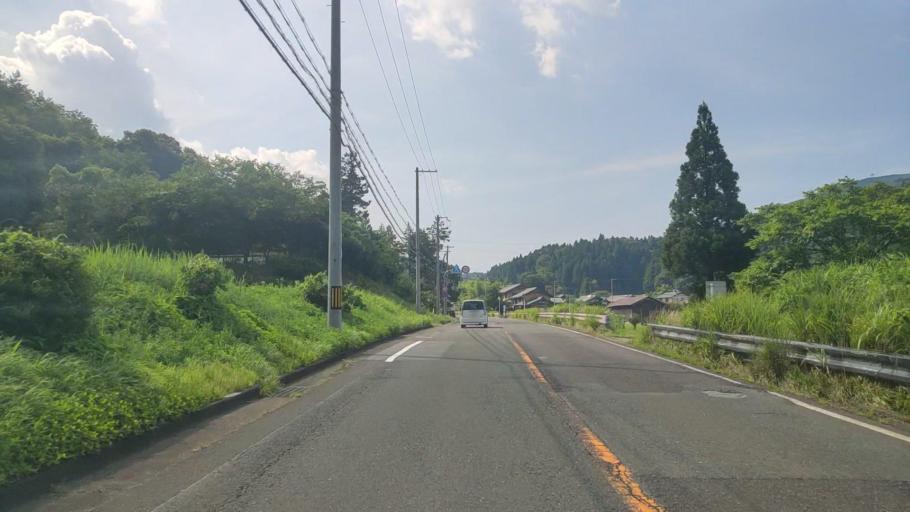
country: JP
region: Fukui
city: Tsuruga
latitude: 35.5530
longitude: 136.1410
